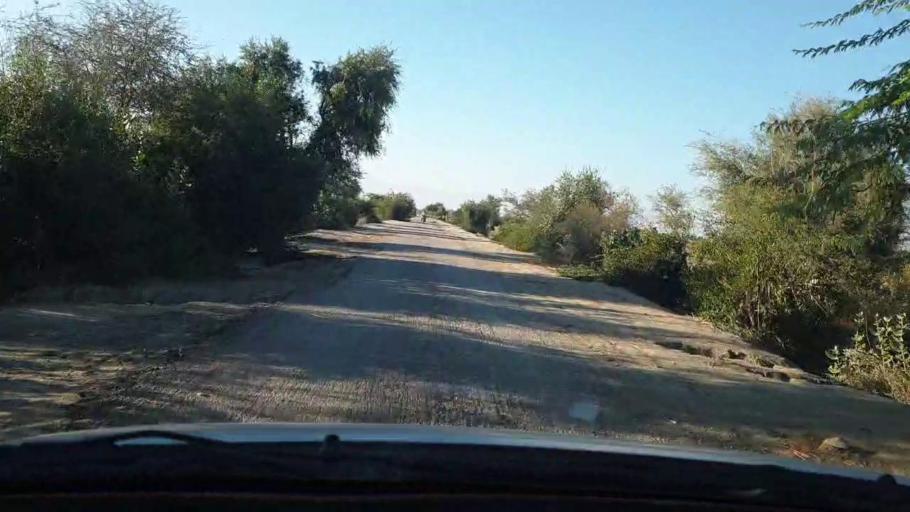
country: PK
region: Sindh
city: Johi
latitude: 26.7680
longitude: 67.4612
